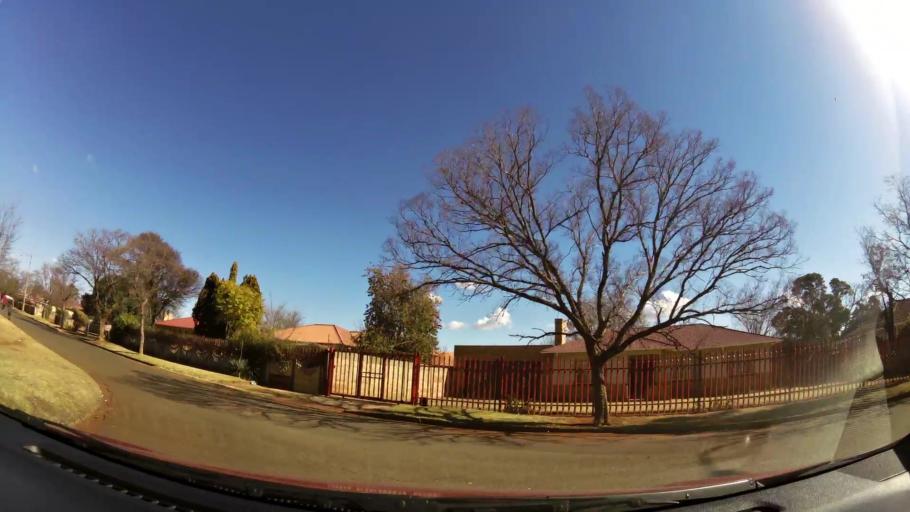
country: ZA
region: Gauteng
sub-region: West Rand District Municipality
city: Carletonville
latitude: -26.3641
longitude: 27.3945
